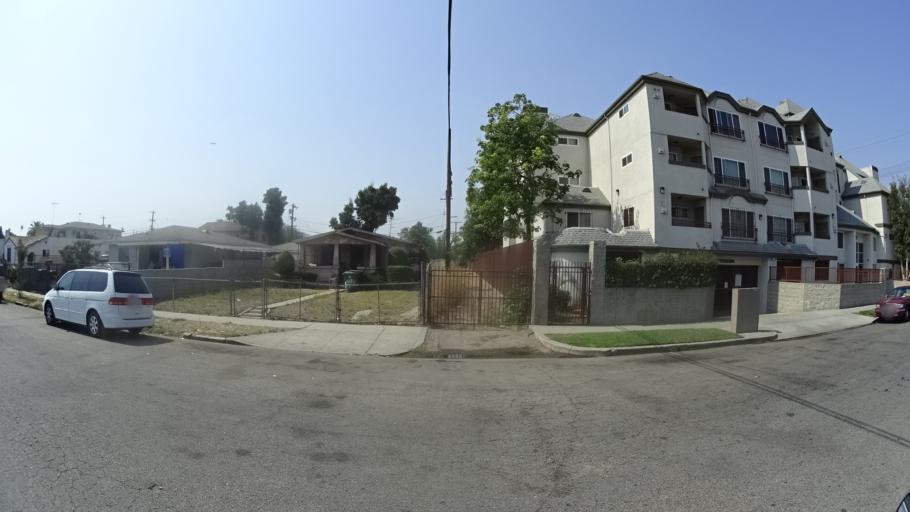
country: US
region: California
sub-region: Los Angeles County
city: Westmont
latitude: 33.9631
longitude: -118.2867
